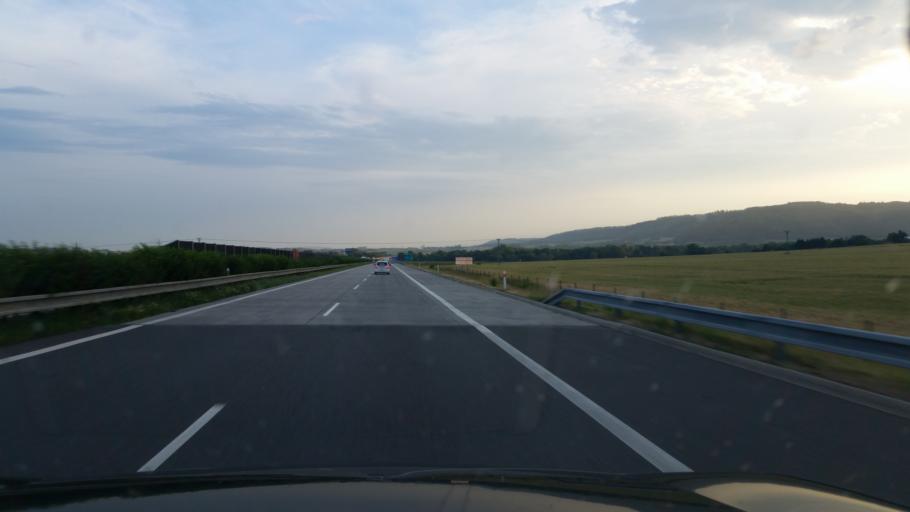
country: CZ
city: Jesenik nad Odrou
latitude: 49.6465
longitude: 17.8786
